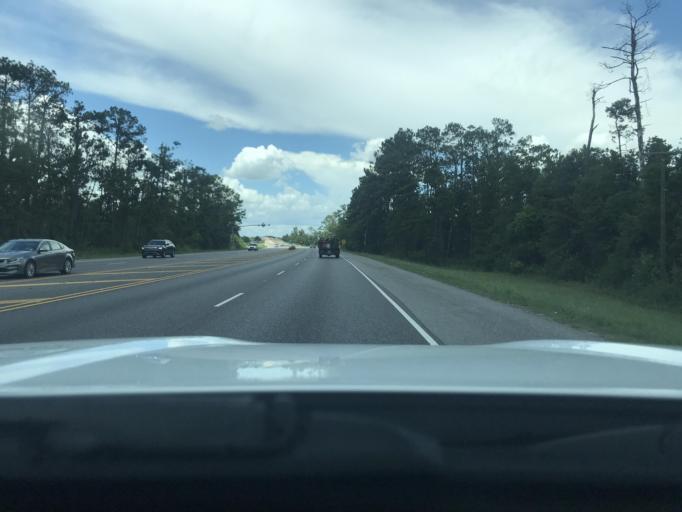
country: US
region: Louisiana
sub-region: Calcasieu Parish
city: Moss Bluff
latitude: 30.2790
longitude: -93.1842
